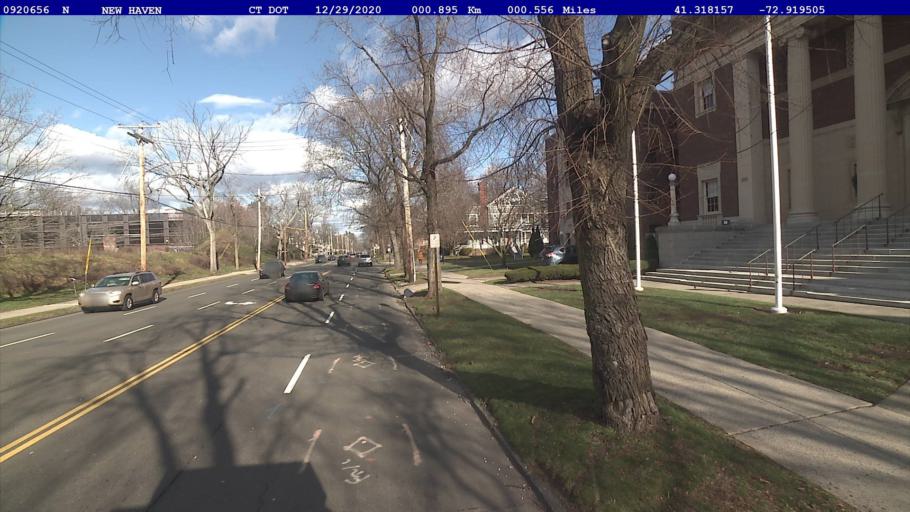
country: US
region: Connecticut
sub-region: New Haven County
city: New Haven
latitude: 41.3182
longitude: -72.9195
